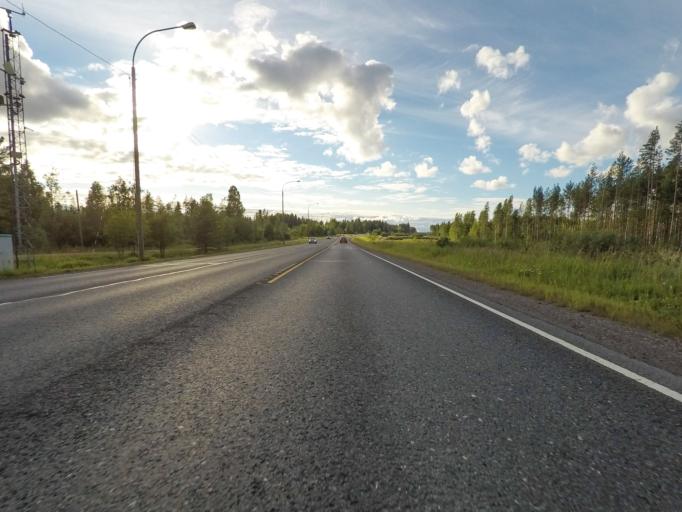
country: FI
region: Northern Savo
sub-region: Kuopio
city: Kuopio
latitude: 62.9592
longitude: 27.8590
